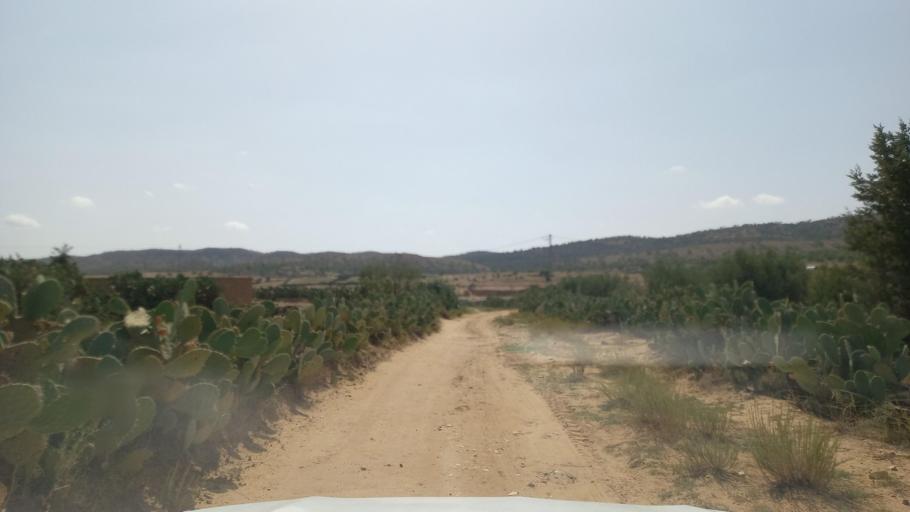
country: TN
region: Al Qasrayn
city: Sbiba
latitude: 35.3862
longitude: 8.9573
